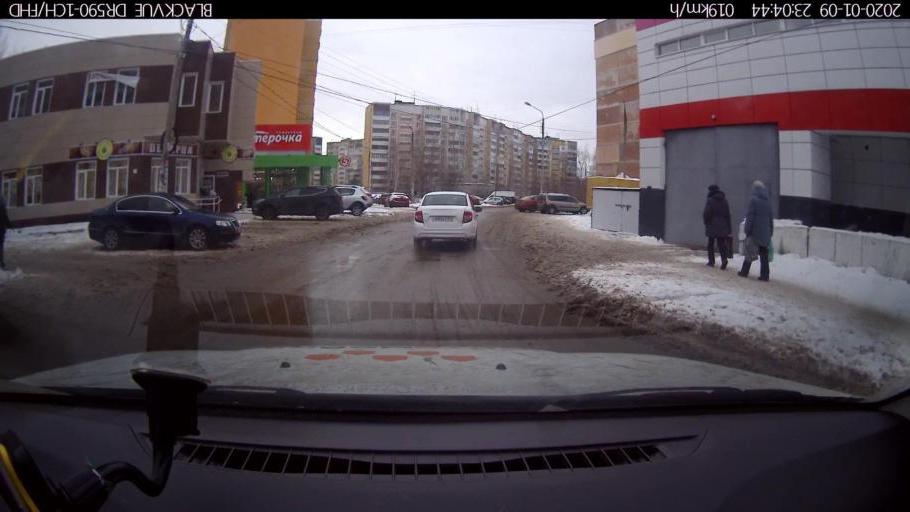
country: RU
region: Nizjnij Novgorod
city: Gorbatovka
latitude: 56.3672
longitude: 43.8055
